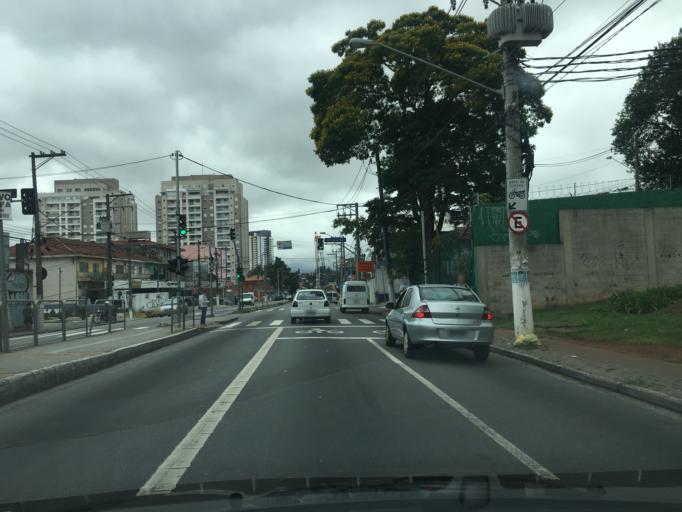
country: BR
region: Sao Paulo
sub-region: Taboao Da Serra
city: Taboao da Serra
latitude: -23.5986
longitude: -46.7412
